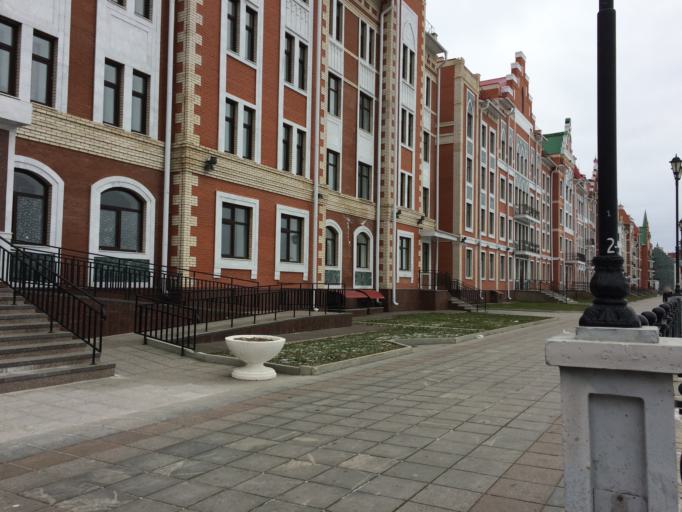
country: RU
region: Mariy-El
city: Yoshkar-Ola
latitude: 56.6362
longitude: 47.9112
